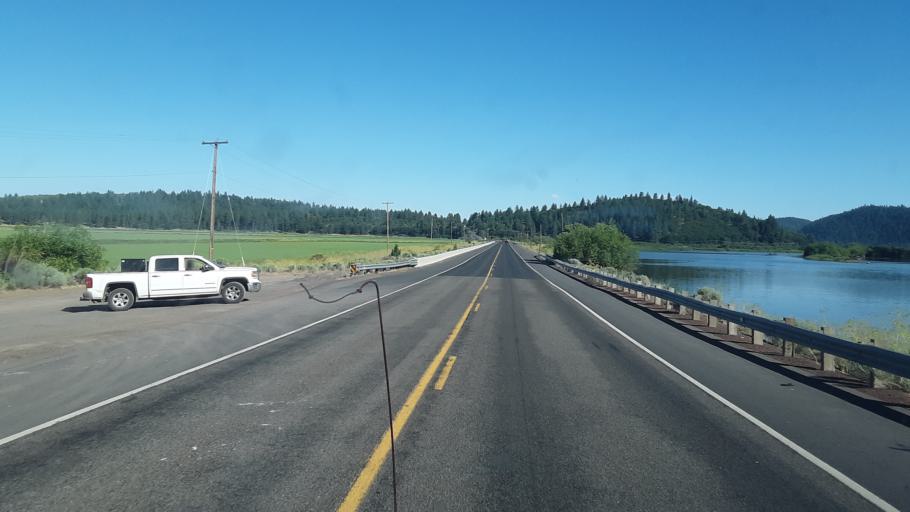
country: US
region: Oregon
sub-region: Klamath County
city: Klamath Falls
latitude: 42.2922
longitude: -121.9287
